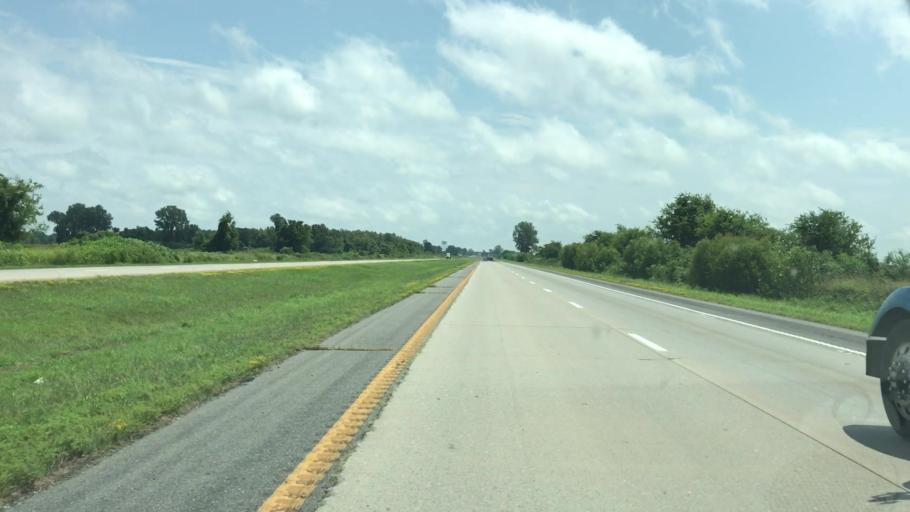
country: US
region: Missouri
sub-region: Pemiscot County
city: Caruthersville
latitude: 36.1717
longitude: -89.6890
